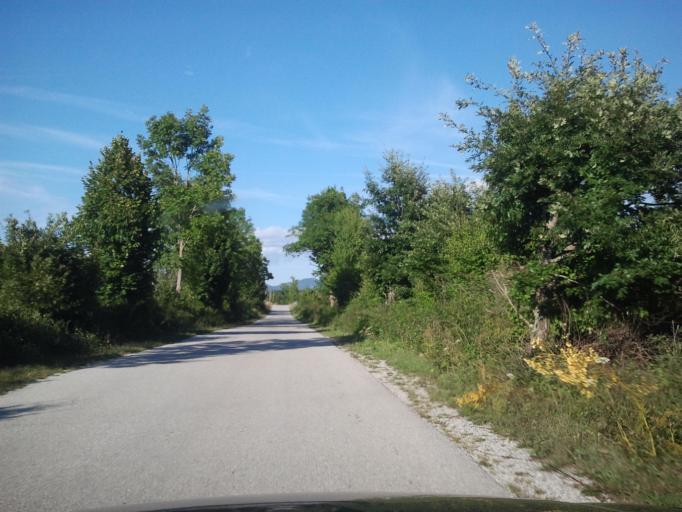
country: HR
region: Zadarska
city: Obrovac
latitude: 44.3548
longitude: 15.6480
